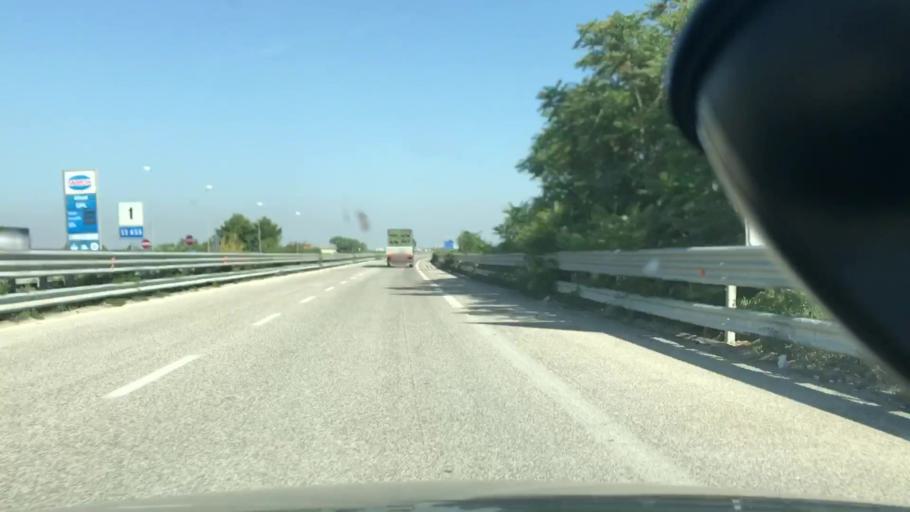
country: IT
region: Apulia
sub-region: Provincia di Foggia
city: Foggia
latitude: 41.4148
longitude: 15.5586
